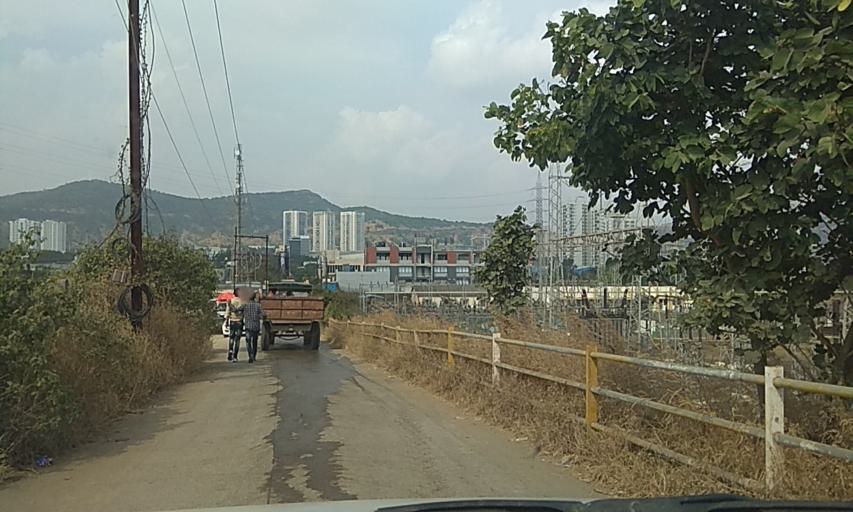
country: IN
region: Maharashtra
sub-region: Pune Division
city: Pimpri
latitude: 18.5871
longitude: 73.7059
